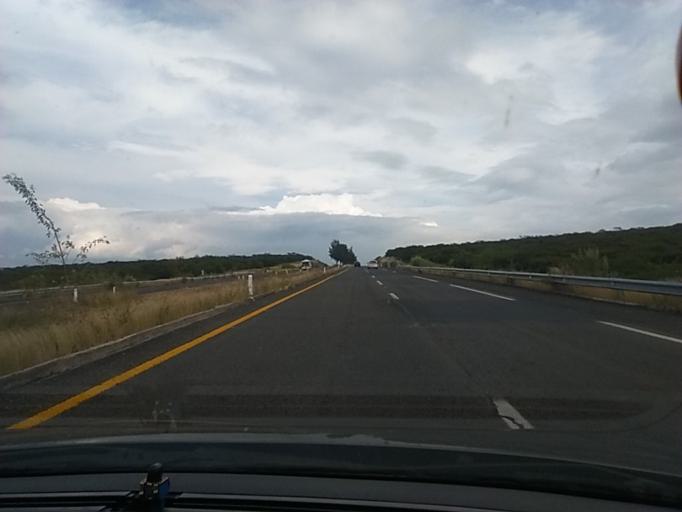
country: MX
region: Michoacan
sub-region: Vista Hermosa
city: La Angostura
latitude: 20.2379
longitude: -102.3963
